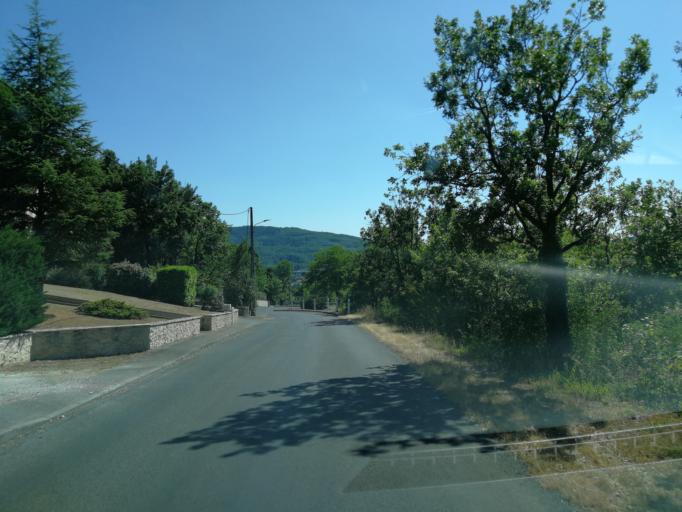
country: FR
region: Midi-Pyrenees
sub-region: Departement du Lot
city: Souillac
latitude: 44.9055
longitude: 1.4798
